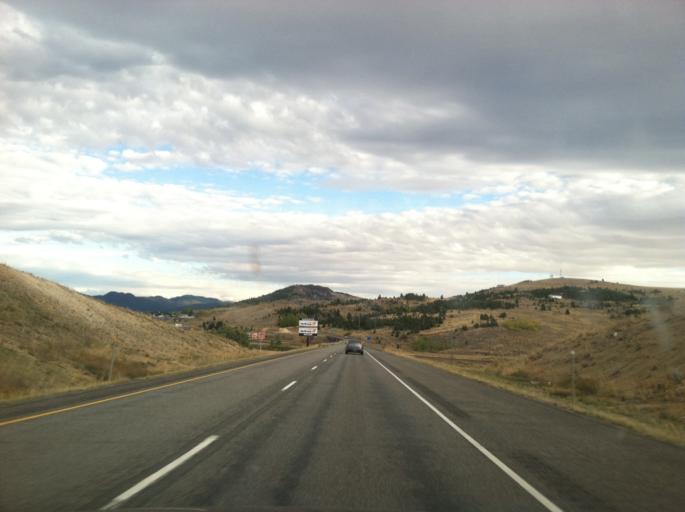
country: US
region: Montana
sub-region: Silver Bow County
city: Butte
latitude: 46.0015
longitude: -112.5704
